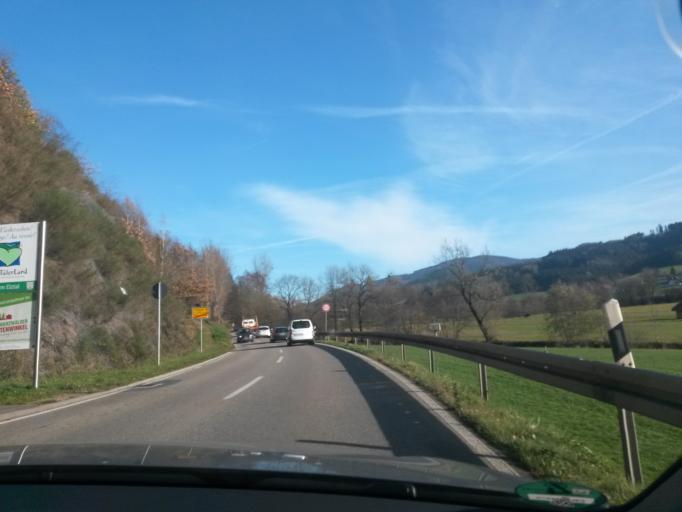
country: DE
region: Baden-Wuerttemberg
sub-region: Freiburg Region
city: Elzach
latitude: 48.1559
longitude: 8.0450
